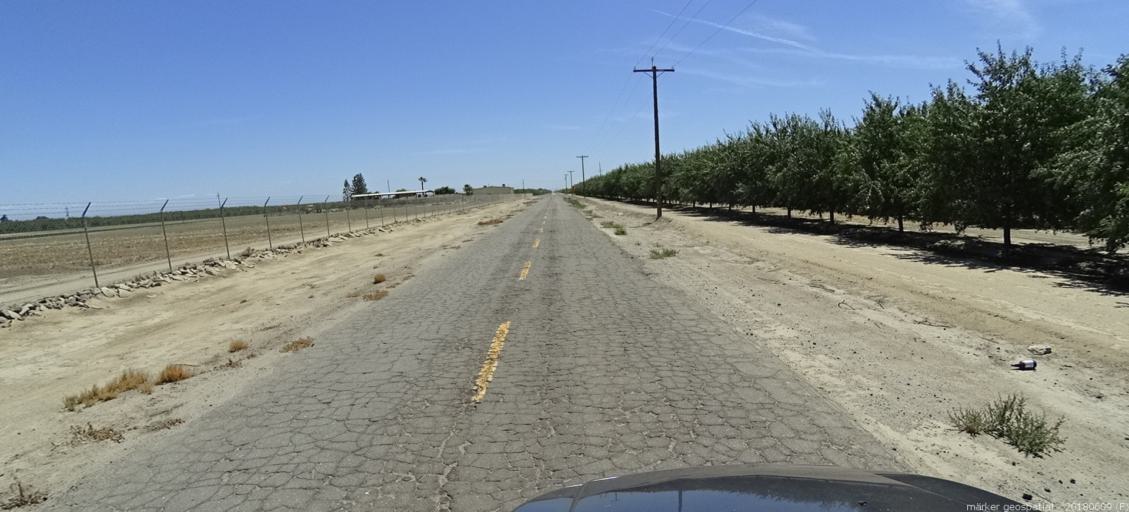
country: US
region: California
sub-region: Madera County
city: Fairmead
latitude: 36.9382
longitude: -120.2053
